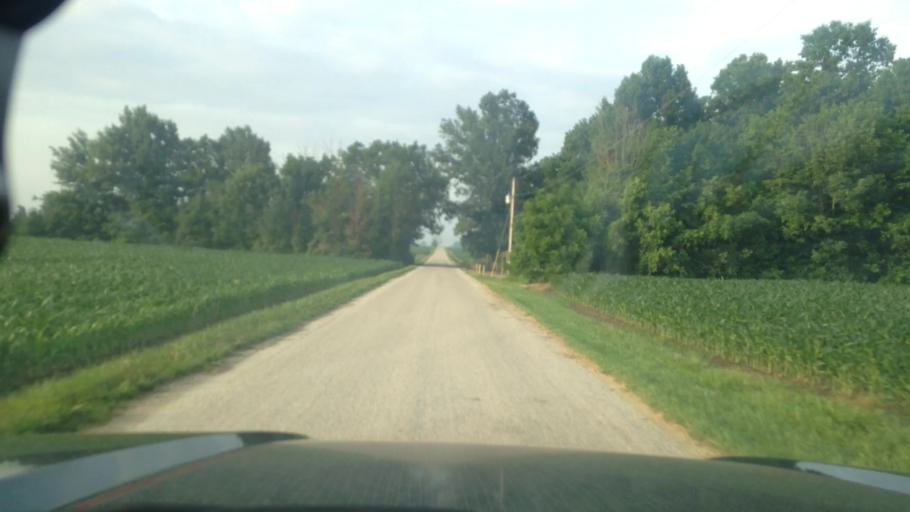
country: US
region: Indiana
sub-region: Randolph County
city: Union City
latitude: 40.2417
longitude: -84.8625
